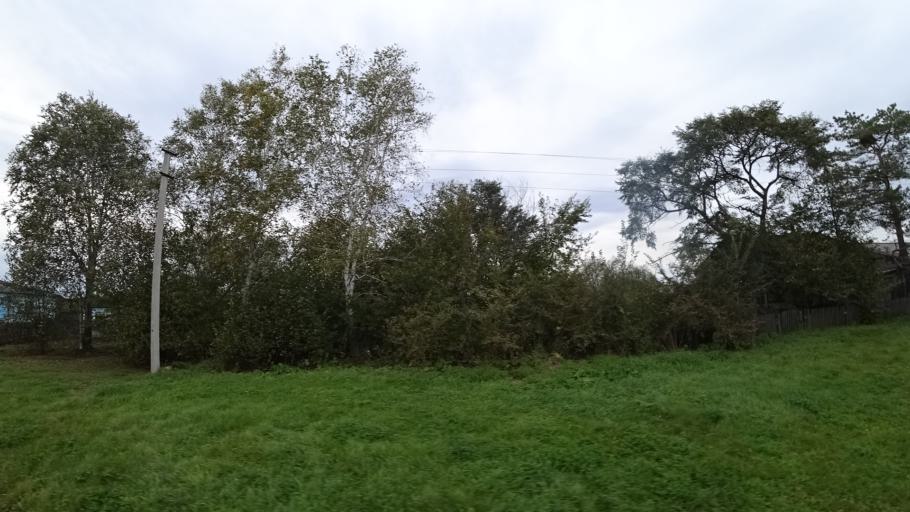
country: RU
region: Amur
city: Arkhara
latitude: 49.4334
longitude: 130.2623
